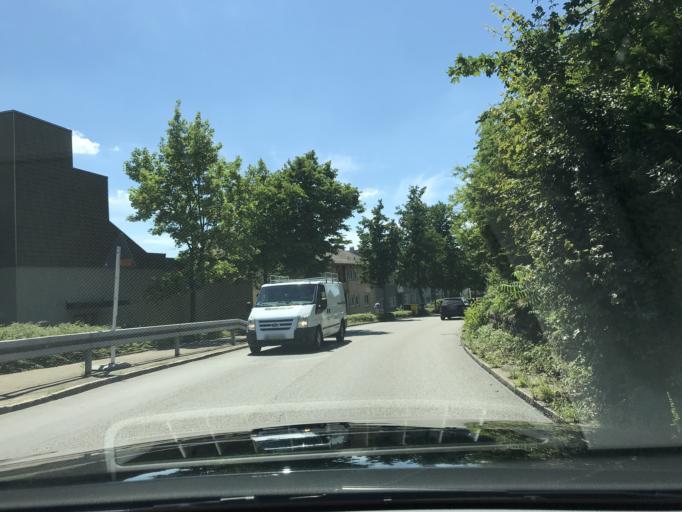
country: DE
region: Baden-Wuerttemberg
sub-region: Regierungsbezirk Stuttgart
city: Waiblingen
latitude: 48.8331
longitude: 9.3298
